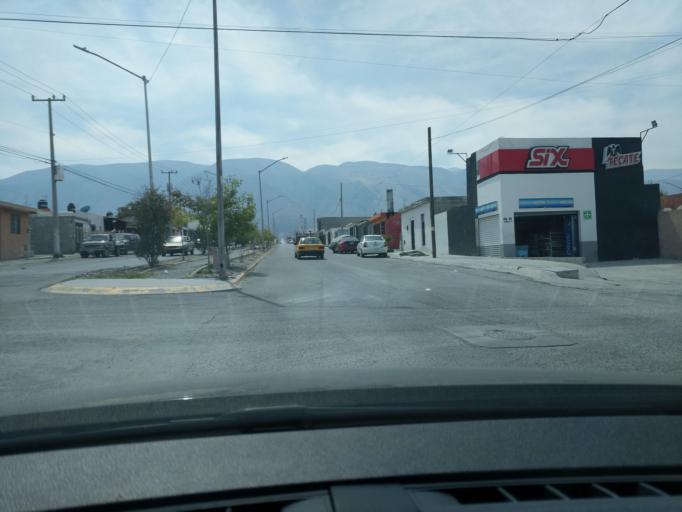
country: MX
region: Coahuila
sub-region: Arteaga
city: Arteaga
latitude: 25.4227
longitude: -100.9018
